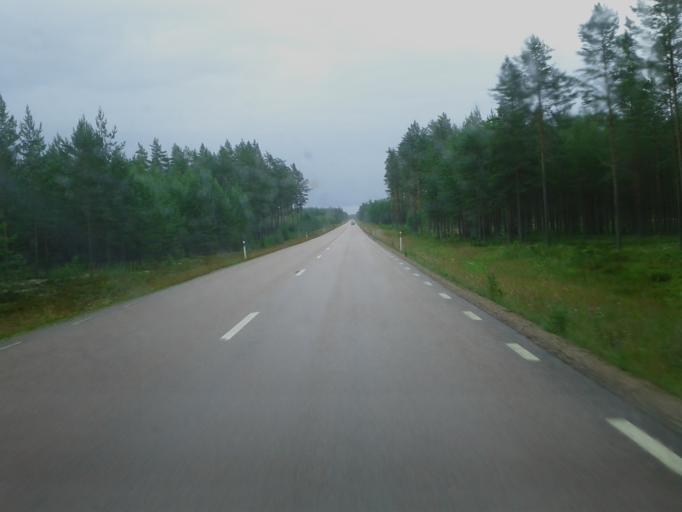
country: SE
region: Dalarna
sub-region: Leksand Municipality
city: Siljansnas
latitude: 60.9358
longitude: 14.7631
